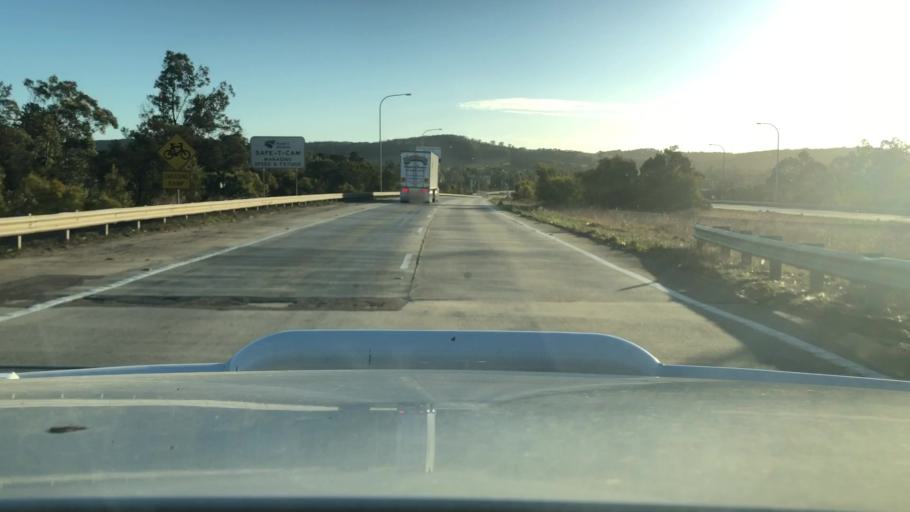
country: AU
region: New South Wales
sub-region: Wingecarribee
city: Bundanoon
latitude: -34.7093
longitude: 150.0109
